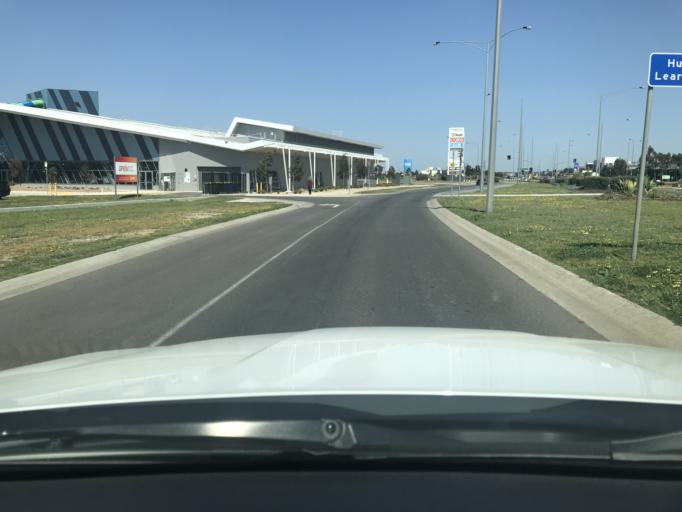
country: AU
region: Victoria
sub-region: Hume
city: Roxburgh Park
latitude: -37.5886
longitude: 144.9111
